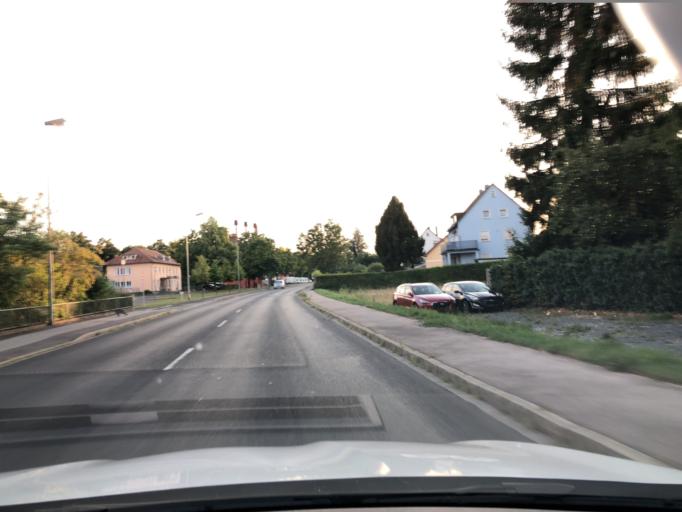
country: DE
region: Bavaria
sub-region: Upper Palatinate
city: Poppenricht
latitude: 49.4907
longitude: 11.7738
